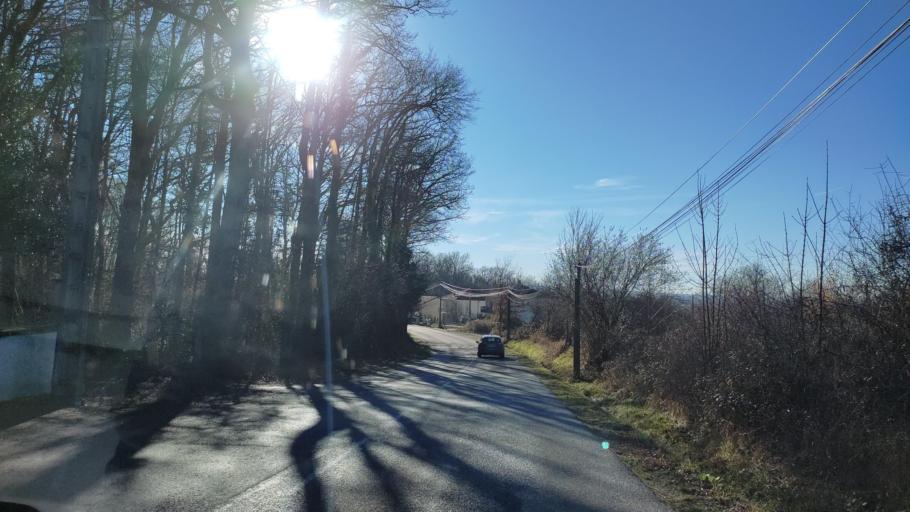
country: FR
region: Limousin
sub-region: Departement de la Haute-Vienne
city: Isle
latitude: 45.8065
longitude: 1.2107
